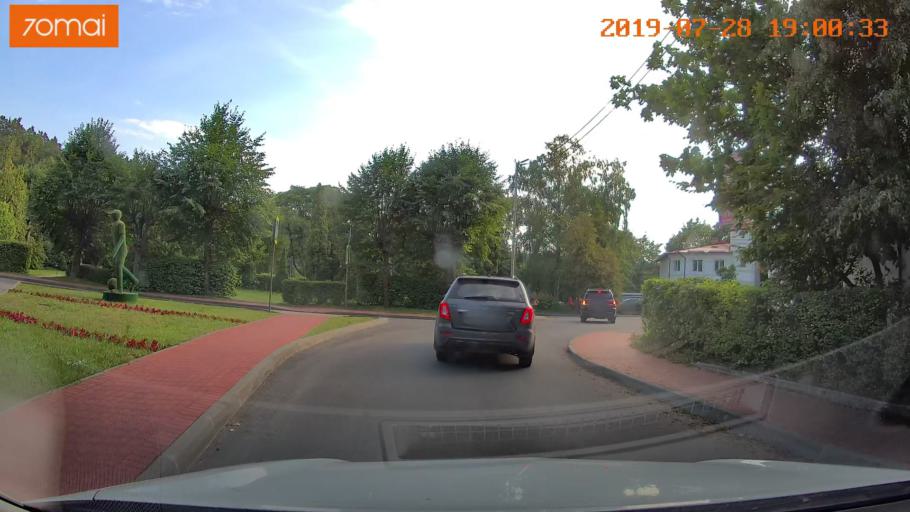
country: RU
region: Kaliningrad
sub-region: Gorod Svetlogorsk
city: Svetlogorsk
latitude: 54.9387
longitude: 20.1585
